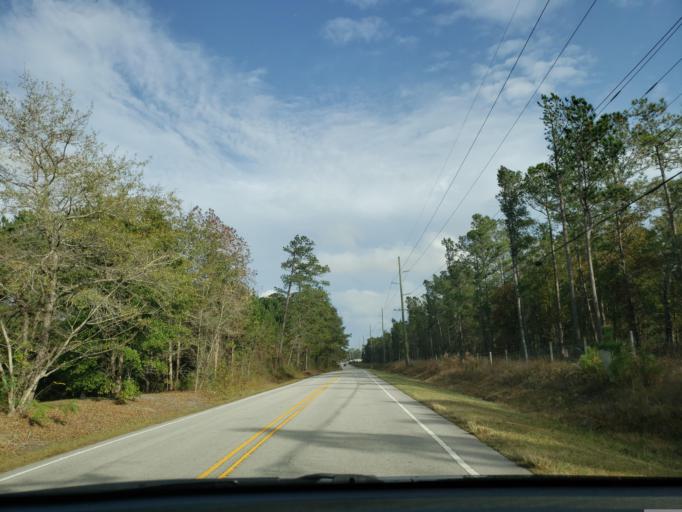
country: US
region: North Carolina
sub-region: Onslow County
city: Jacksonville
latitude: 34.6859
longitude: -77.5193
